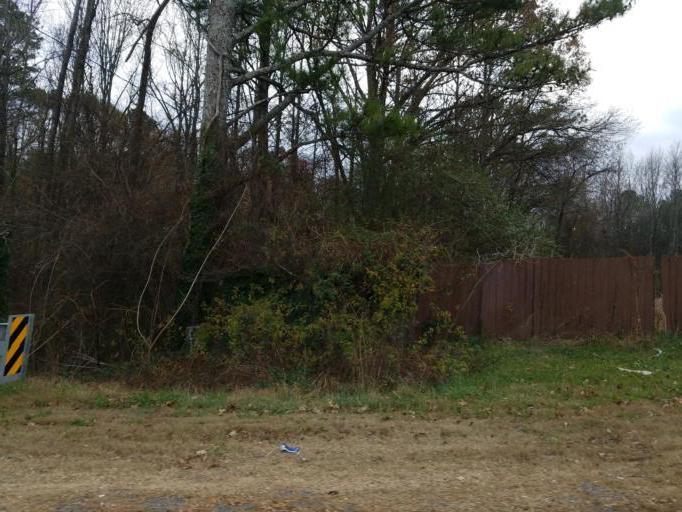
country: US
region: Georgia
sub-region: Cherokee County
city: Canton
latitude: 34.2119
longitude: -84.5265
